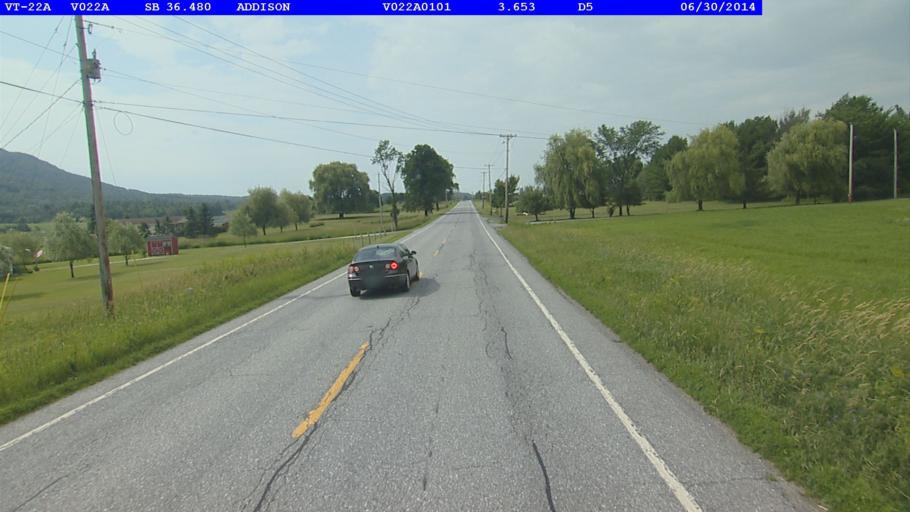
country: US
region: Vermont
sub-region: Addison County
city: Vergennes
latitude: 44.0821
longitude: -73.3030
